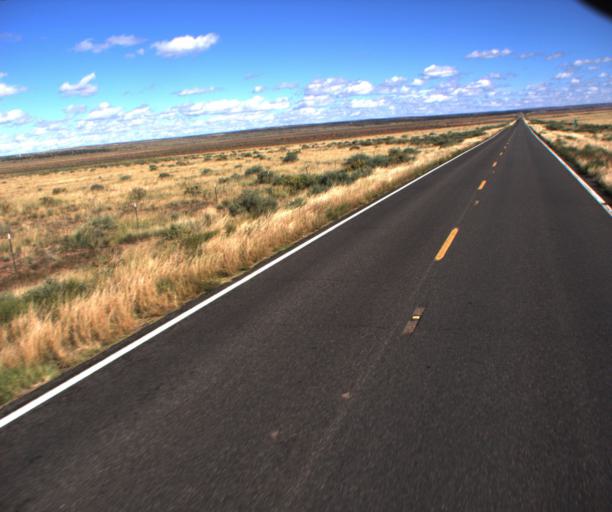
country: US
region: Arizona
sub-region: Apache County
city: Saint Johns
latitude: 34.6815
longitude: -109.2819
